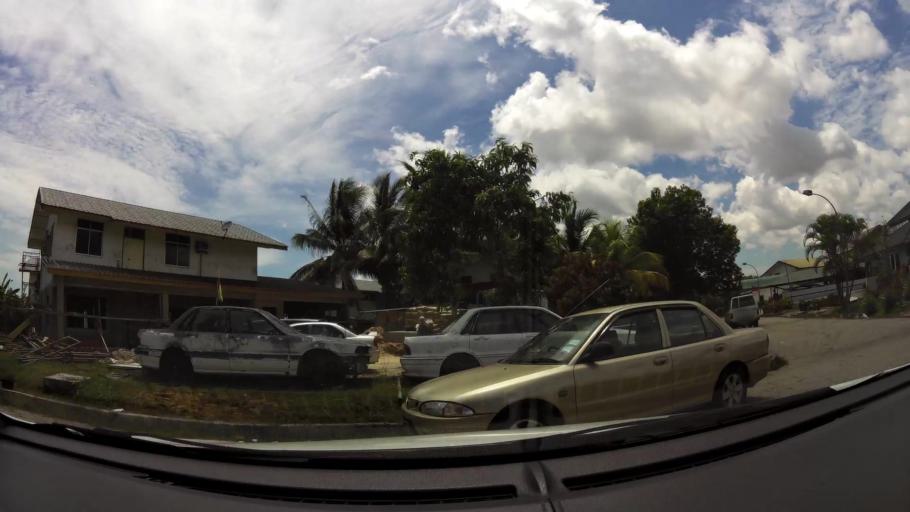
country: BN
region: Brunei and Muara
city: Bandar Seri Begawan
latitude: 4.9570
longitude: 114.9015
